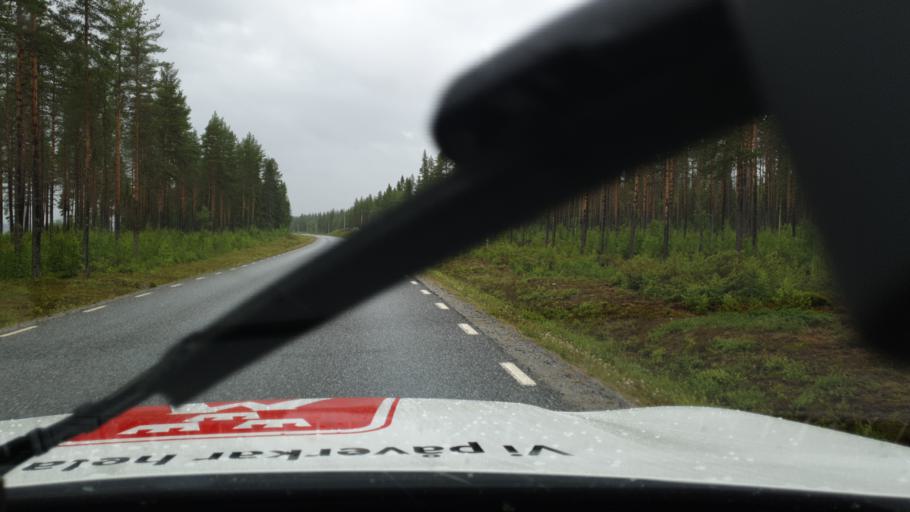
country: SE
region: Vaesterbotten
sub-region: Vilhelmina Kommun
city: Vilhelmina
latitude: 64.3799
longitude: 16.8990
